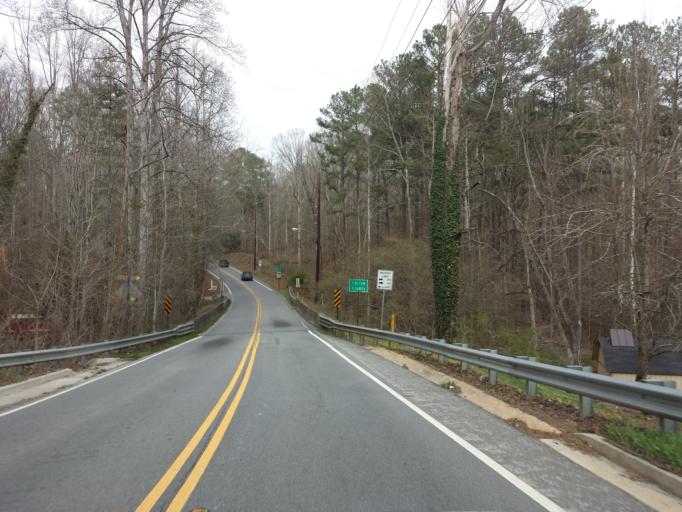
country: US
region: Georgia
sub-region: Fulton County
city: Roswell
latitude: 34.0378
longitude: -84.4086
